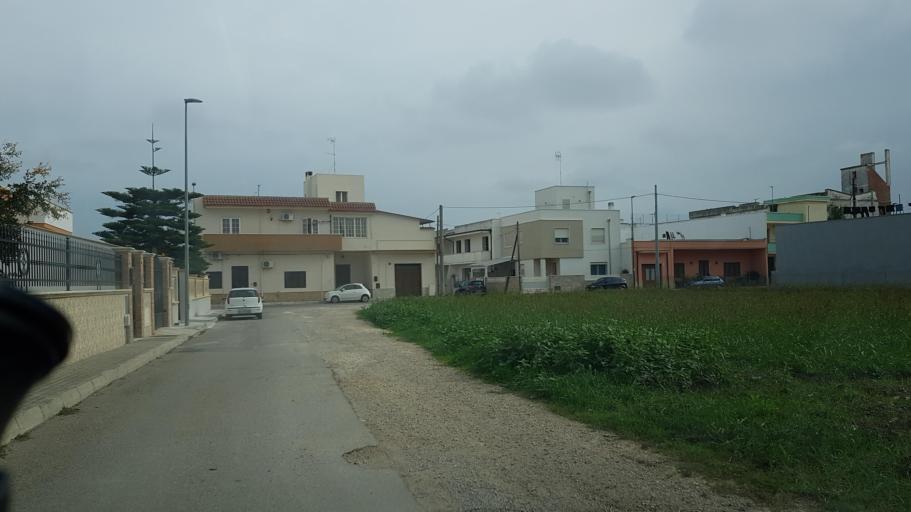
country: IT
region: Apulia
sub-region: Provincia di Lecce
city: Guagnano
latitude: 40.4044
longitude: 17.9424
